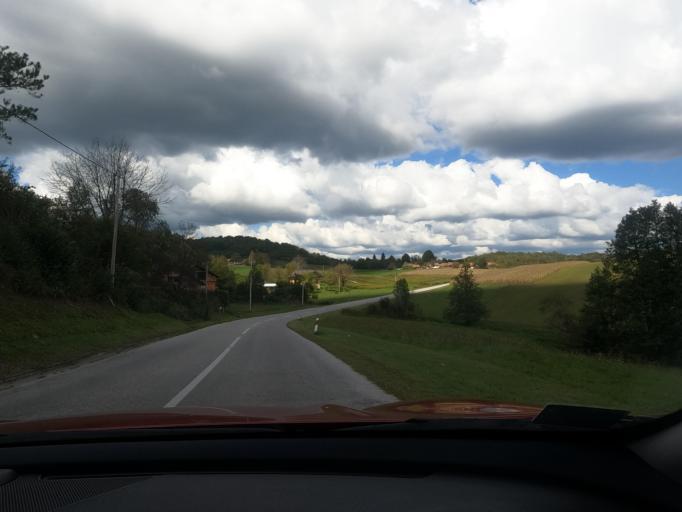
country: BA
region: Federation of Bosnia and Herzegovina
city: Velika Kladusa
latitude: 45.2195
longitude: 15.7282
